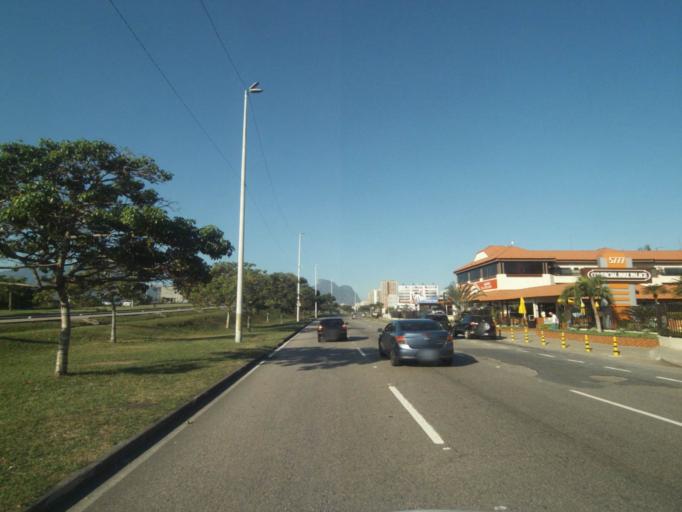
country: BR
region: Rio de Janeiro
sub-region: Rio De Janeiro
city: Rio de Janeiro
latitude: -23.0005
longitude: -43.3712
